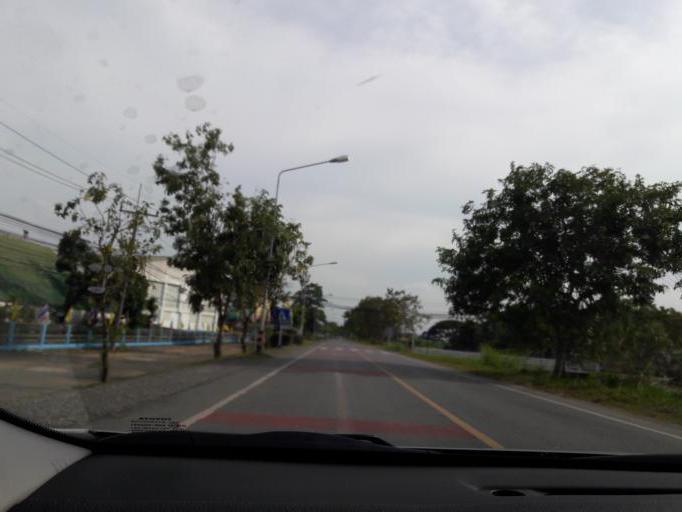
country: TH
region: Ang Thong
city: Ang Thong
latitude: 14.5842
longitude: 100.4442
